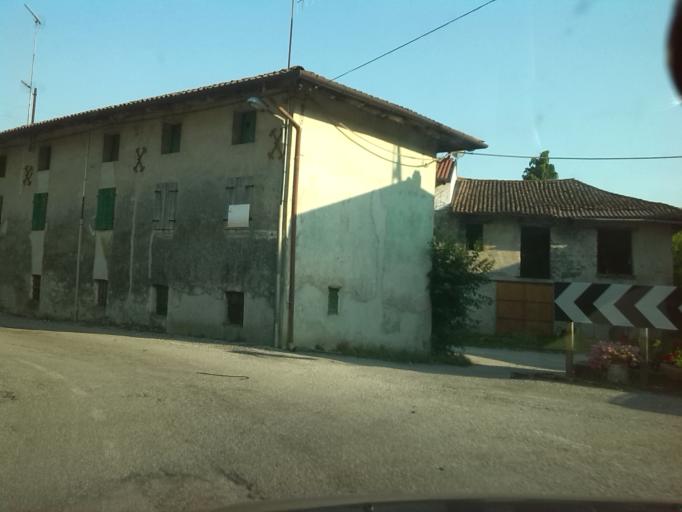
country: IT
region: Friuli Venezia Giulia
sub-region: Provincia di Gorizia
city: Dolegna del Collio
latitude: 46.0318
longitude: 13.4754
